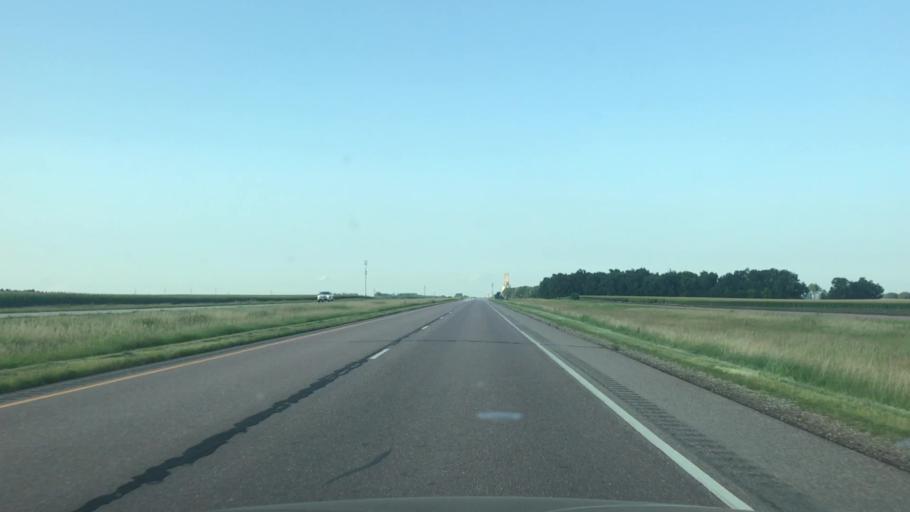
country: US
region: Minnesota
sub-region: Jackson County
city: Lakefield
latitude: 43.7556
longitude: -95.3837
